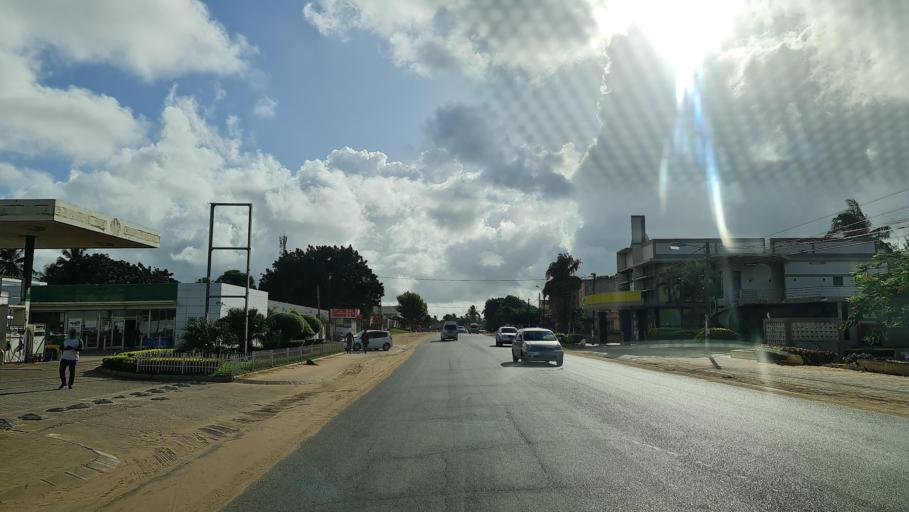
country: MZ
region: Gaza
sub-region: Xai-Xai District
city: Xai-Xai
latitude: -25.0564
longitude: 33.6651
